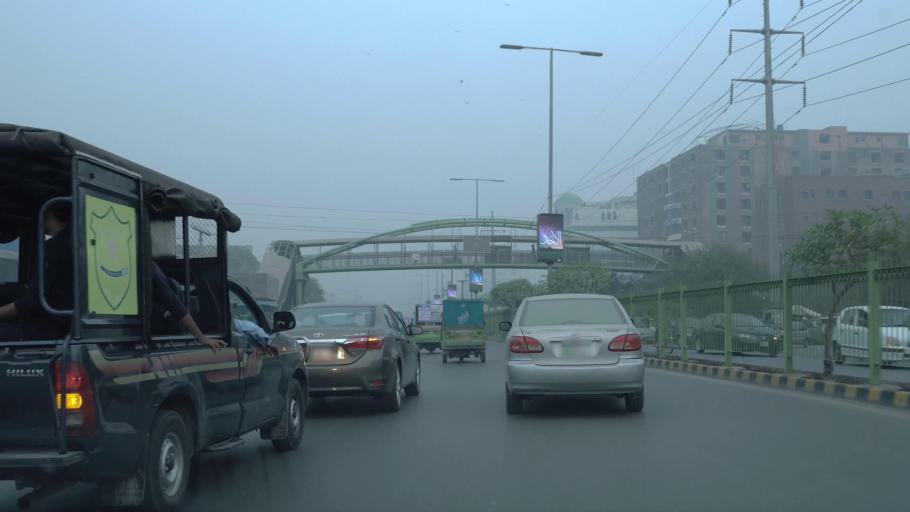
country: PK
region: Punjab
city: Lahore
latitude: 31.5007
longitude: 74.3192
